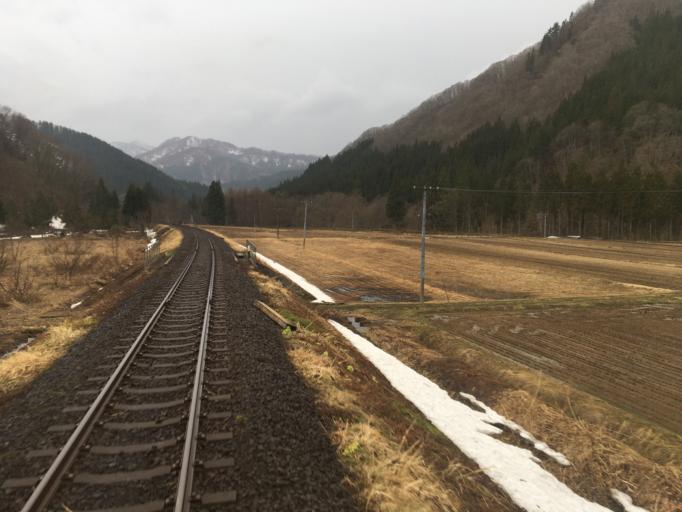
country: JP
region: Akita
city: Kakunodatemachi
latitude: 39.9049
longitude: 140.4744
